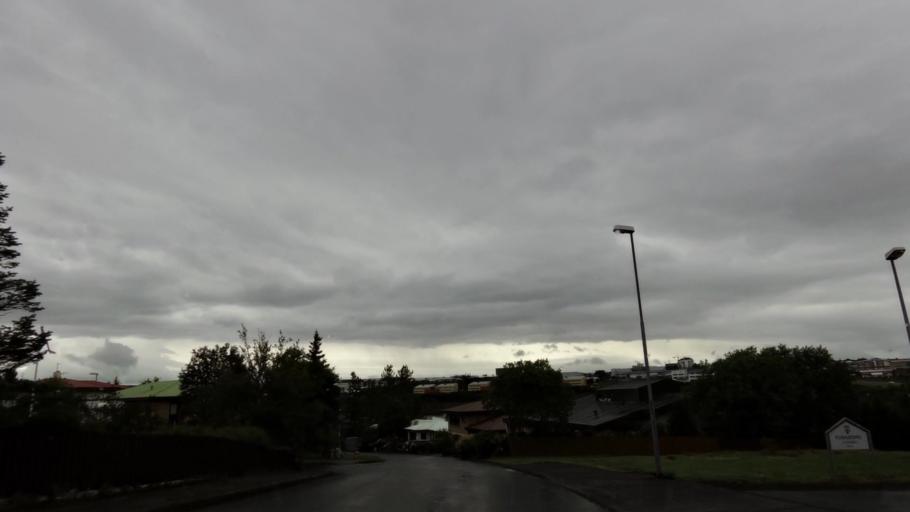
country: IS
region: Capital Region
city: Reykjavik
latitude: 64.1350
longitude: -21.8089
